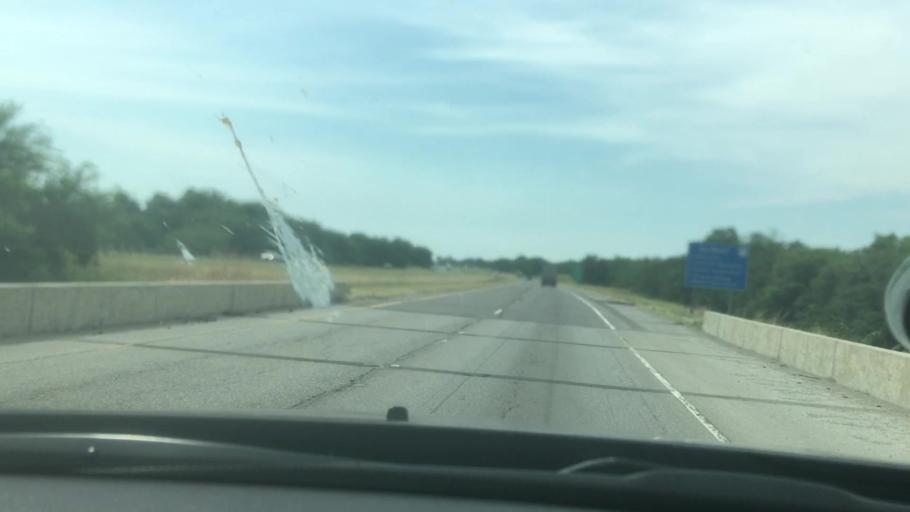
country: US
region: Oklahoma
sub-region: Murray County
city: Davis
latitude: 34.5256
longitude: -97.1855
